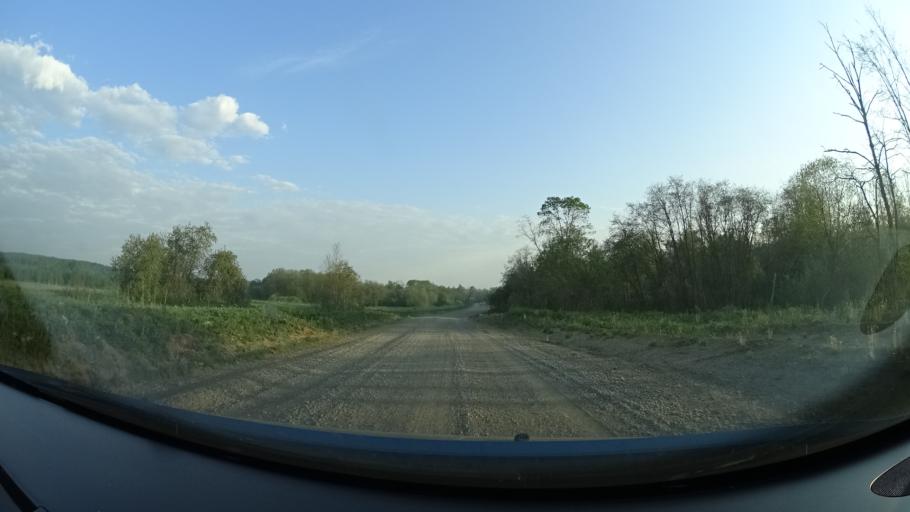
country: RU
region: Perm
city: Kuyeda
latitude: 56.6381
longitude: 55.7080
